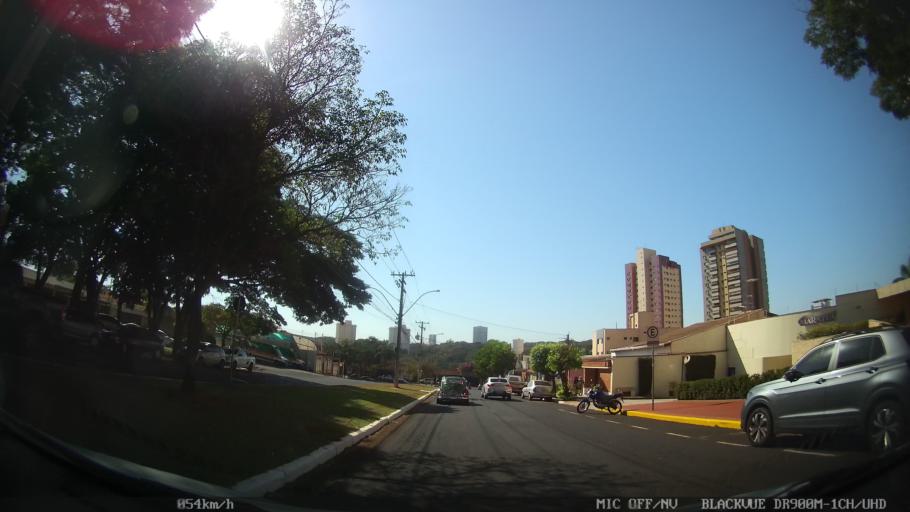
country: BR
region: Sao Paulo
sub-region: Ribeirao Preto
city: Ribeirao Preto
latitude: -21.1995
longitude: -47.8006
